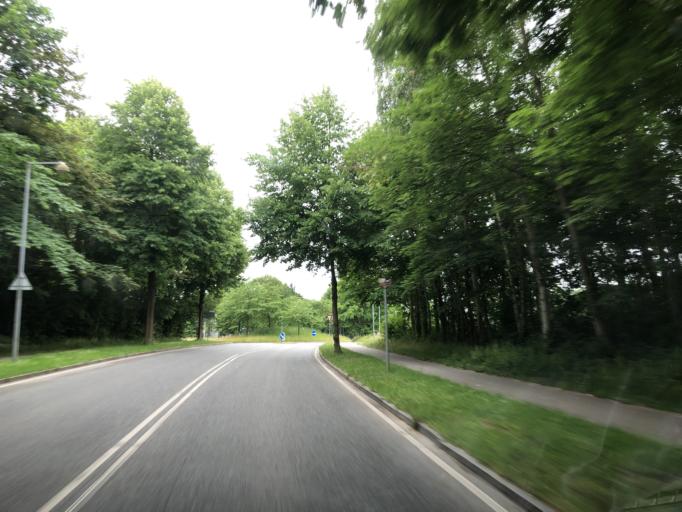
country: DK
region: Capital Region
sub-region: Lyngby-Tarbaek Kommune
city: Kongens Lyngby
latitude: 55.8032
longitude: 12.5007
